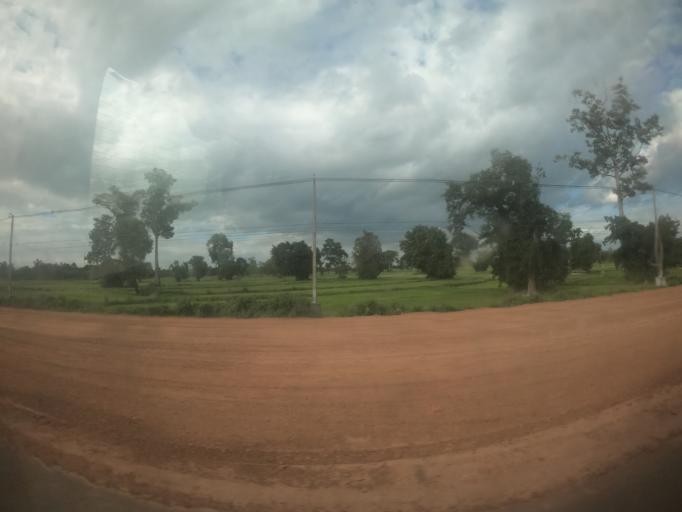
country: TH
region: Surin
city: Kap Choeng
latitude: 14.5029
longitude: 103.5608
